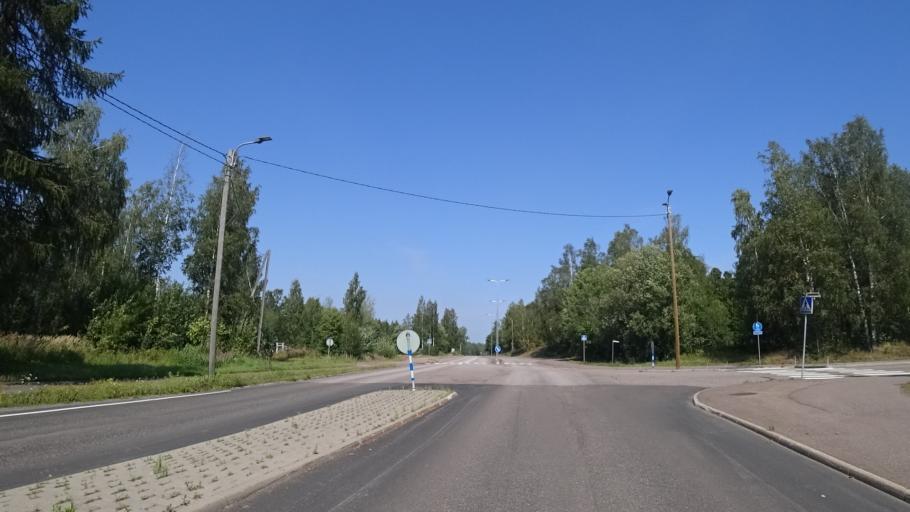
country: FI
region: Kymenlaakso
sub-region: Kotka-Hamina
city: Karhula
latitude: 60.5064
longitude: 26.9467
